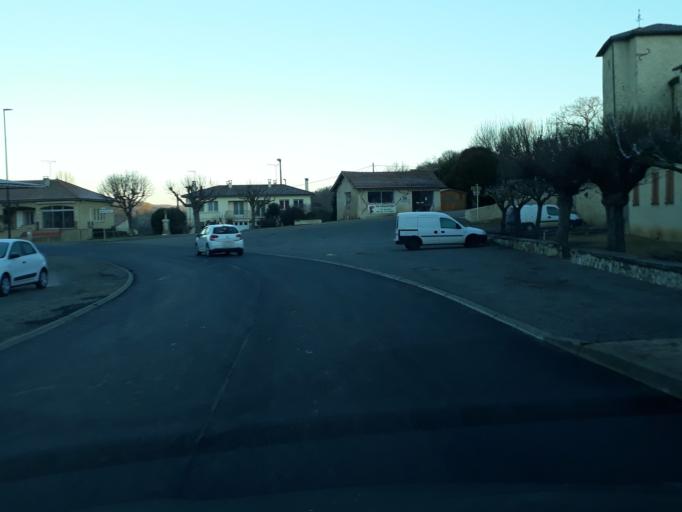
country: FR
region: Midi-Pyrenees
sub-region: Departement du Gers
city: Pavie
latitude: 43.6204
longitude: 0.6479
